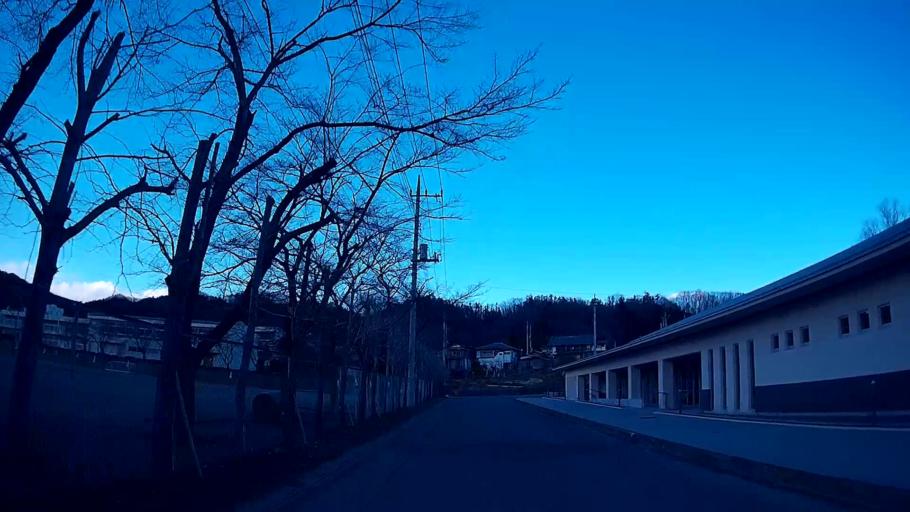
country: JP
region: Saitama
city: Chichibu
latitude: 36.0289
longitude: 138.9874
